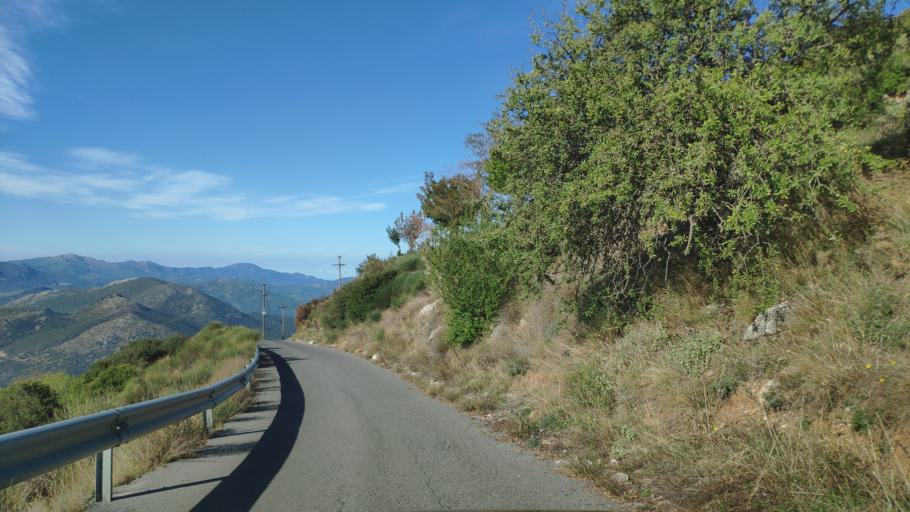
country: GR
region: Peloponnese
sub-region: Nomos Arkadias
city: Dimitsana
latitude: 37.5496
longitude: 22.0677
